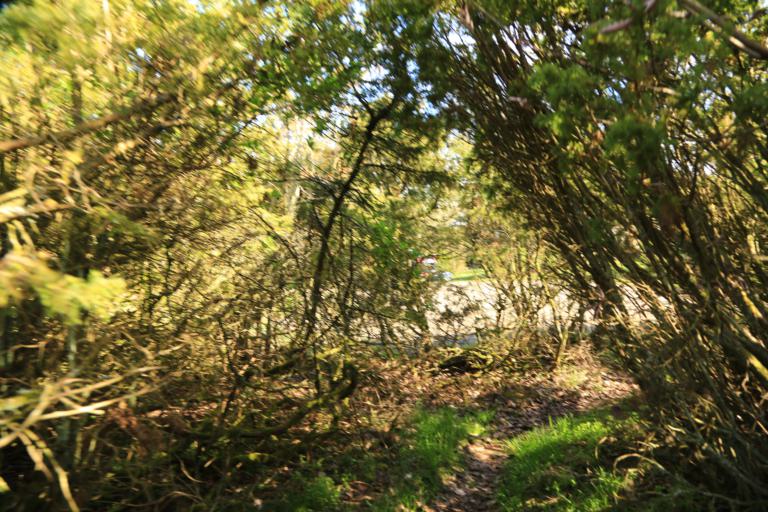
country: SE
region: Halland
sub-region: Varbergs Kommun
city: Varberg
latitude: 57.0850
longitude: 12.2606
